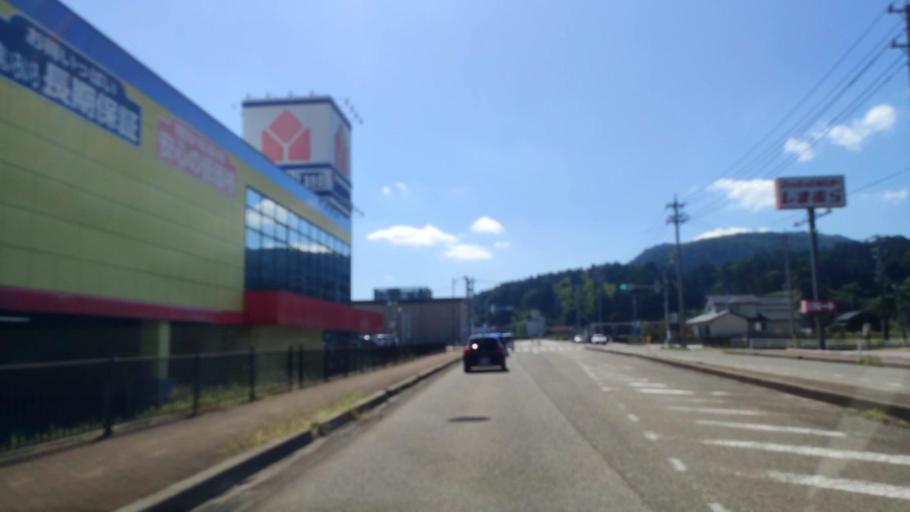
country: JP
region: Ishikawa
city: Nanao
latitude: 37.3859
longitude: 136.9026
